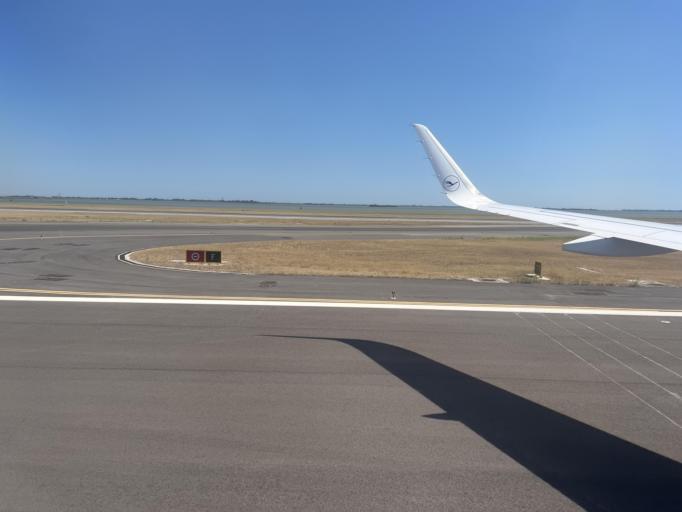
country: IT
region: Veneto
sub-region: Provincia di Venezia
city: Tessera
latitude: 45.5091
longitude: 12.3534
